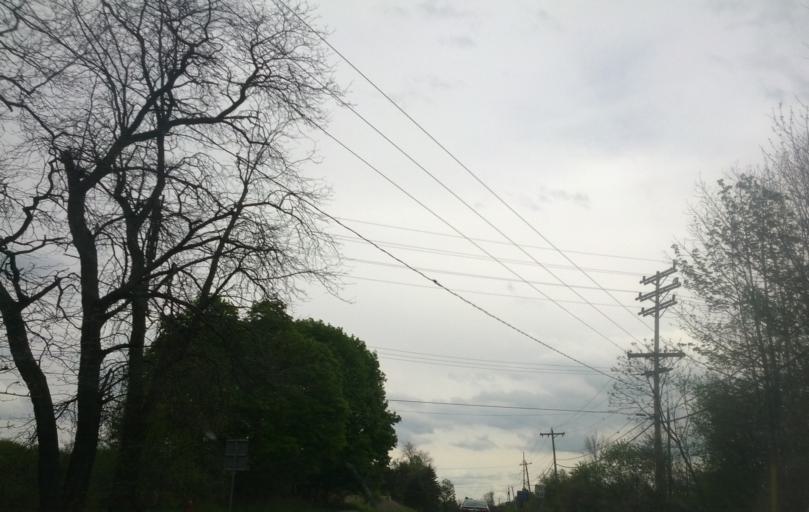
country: US
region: New York
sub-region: Onondaga County
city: Nedrow
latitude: 42.9998
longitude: -76.1263
